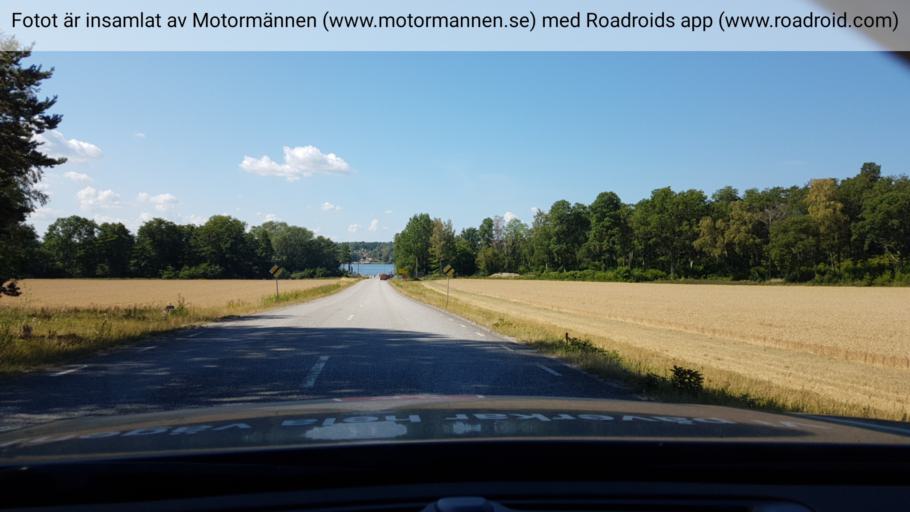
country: SE
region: Stockholm
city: Stenhamra
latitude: 59.3937
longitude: 17.5401
